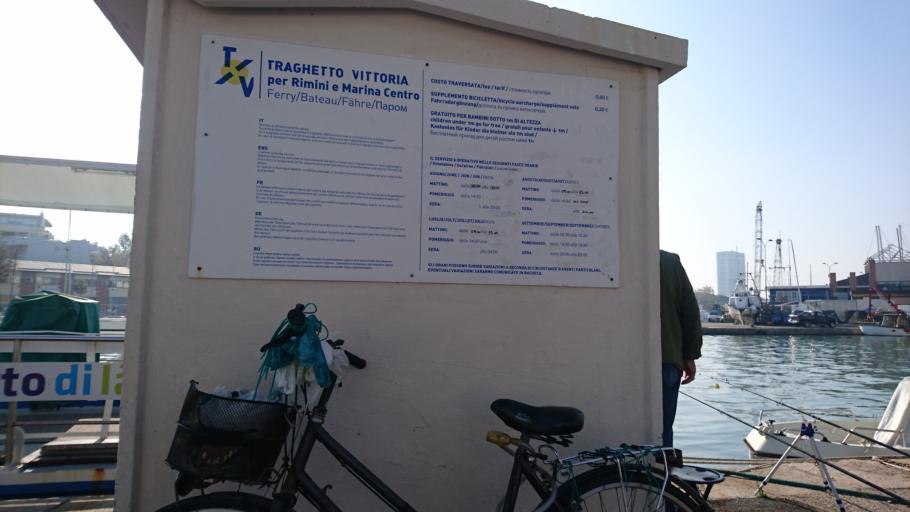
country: IT
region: Emilia-Romagna
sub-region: Provincia di Rimini
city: Rimini
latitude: 44.0748
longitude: 12.5733
